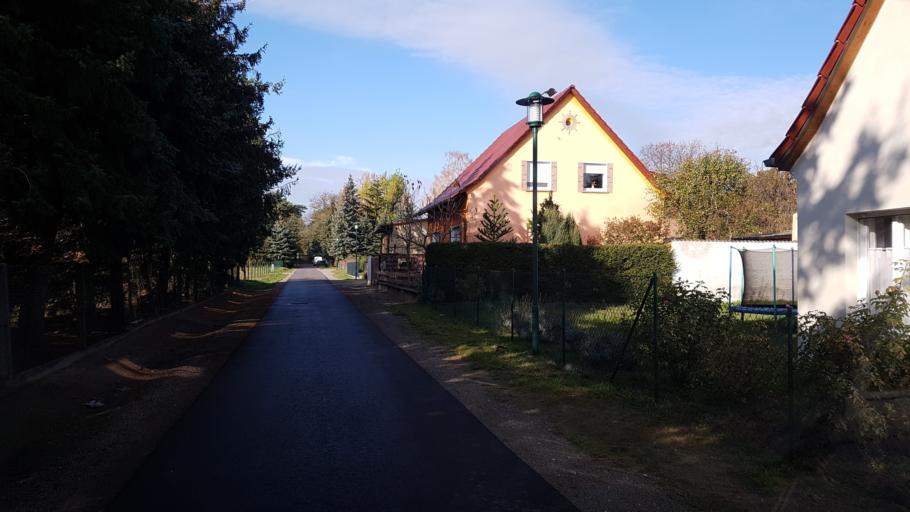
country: DE
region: Brandenburg
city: Doberlug-Kirchhain
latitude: 51.6921
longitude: 13.5090
